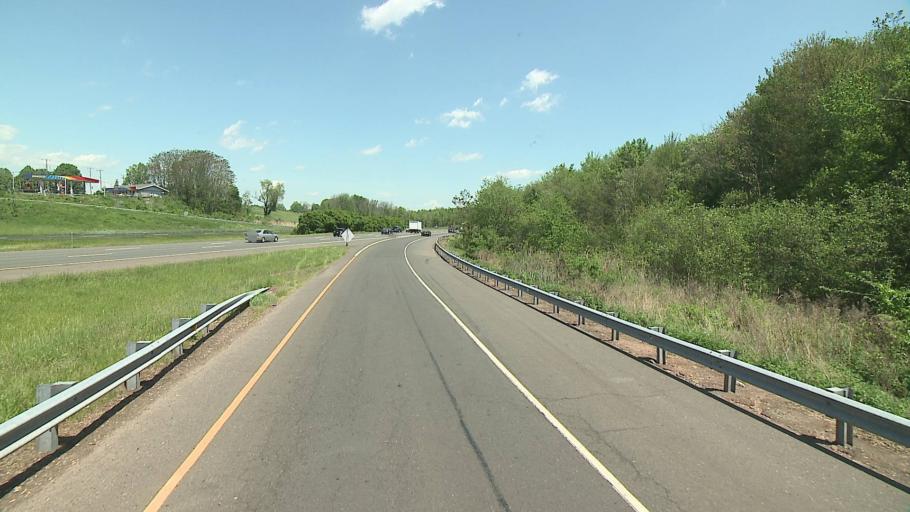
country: US
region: Connecticut
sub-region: Hartford County
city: Plainville
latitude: 41.6127
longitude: -72.8980
